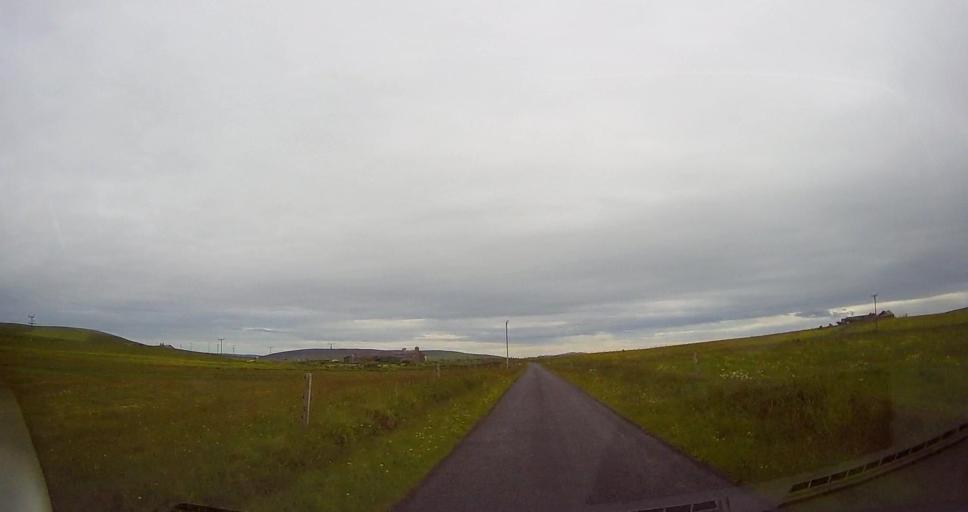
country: GB
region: Scotland
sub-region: Orkney Islands
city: Stromness
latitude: 59.1235
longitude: -3.2783
